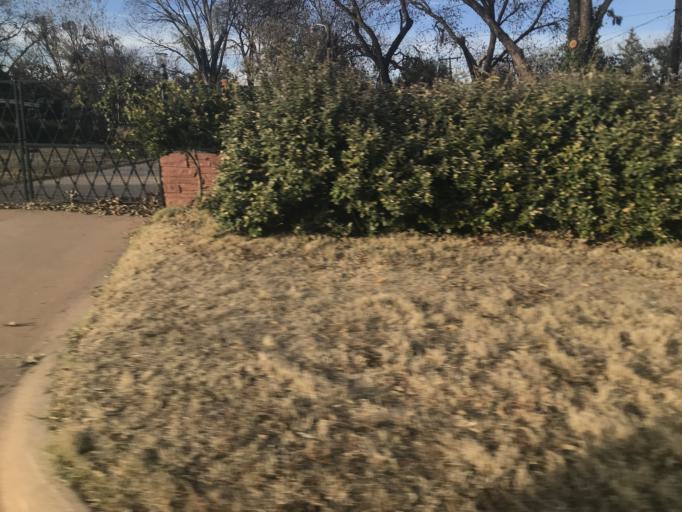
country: US
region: Texas
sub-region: Taylor County
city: Abilene
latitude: 32.4324
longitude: -99.7710
